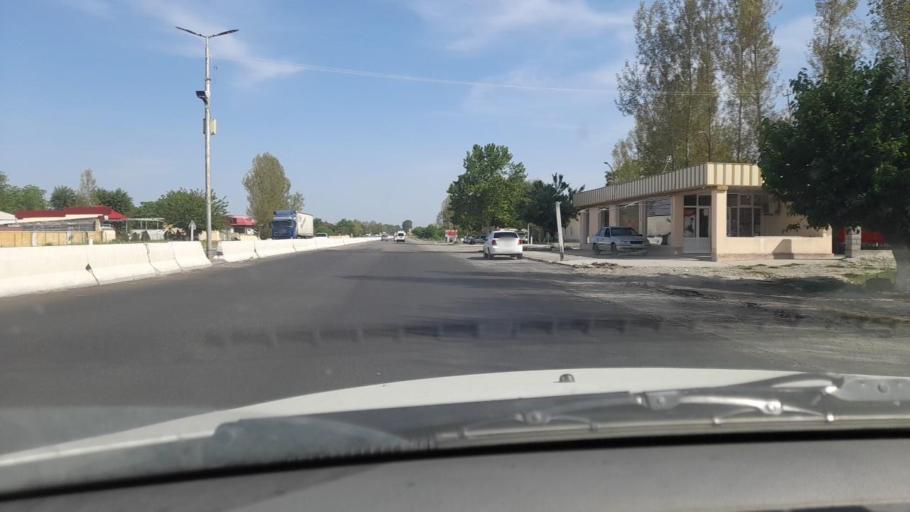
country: UZ
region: Samarqand
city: Chelak
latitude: 39.8404
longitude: 66.8190
